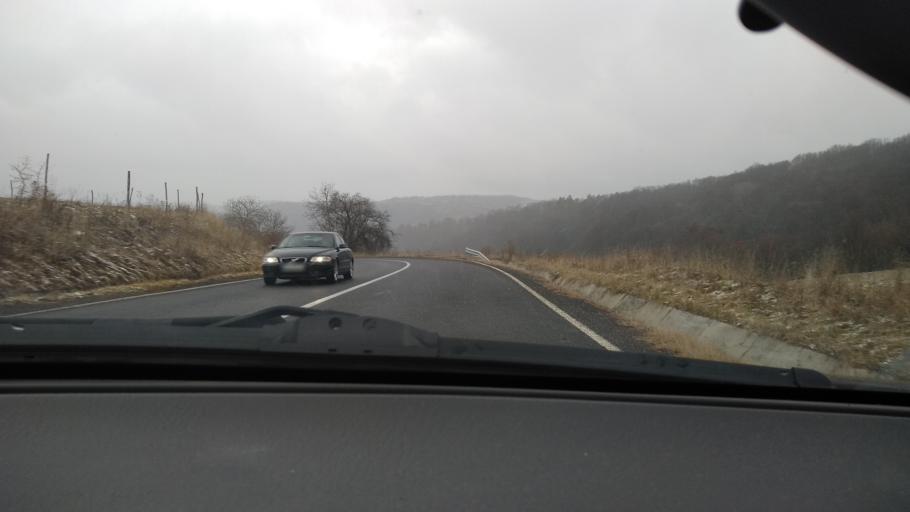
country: RO
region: Mures
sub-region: Comuna Chibed
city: Chibed
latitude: 46.5808
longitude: 24.9564
